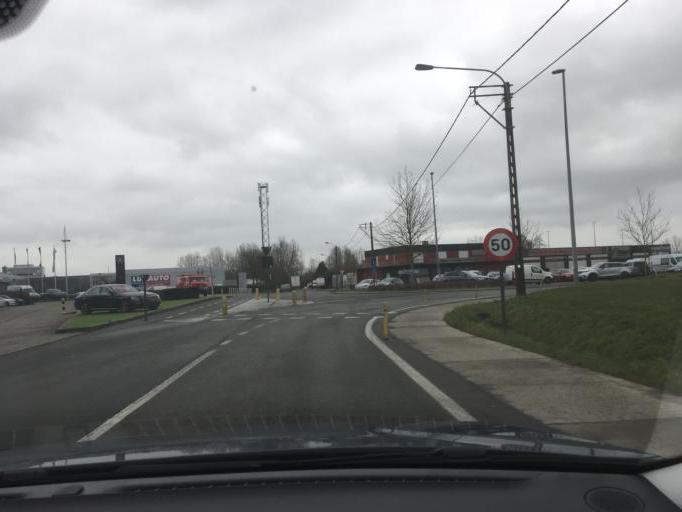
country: BE
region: Flanders
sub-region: Provincie West-Vlaanderen
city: Waregem
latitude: 50.8745
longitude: 3.4416
